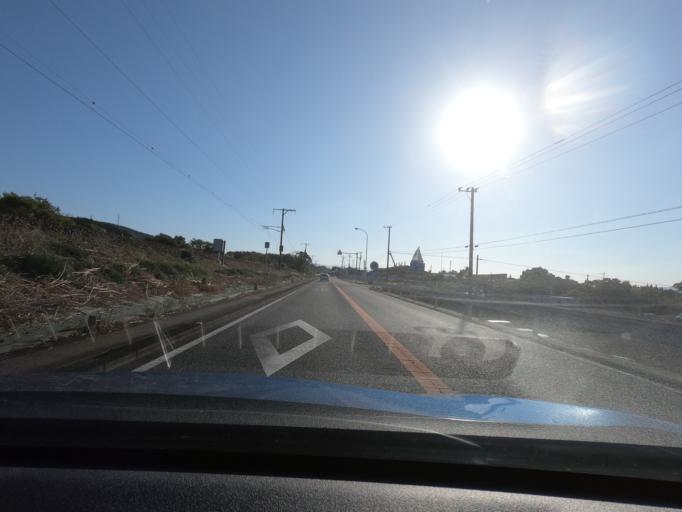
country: JP
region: Kagoshima
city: Izumi
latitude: 32.1439
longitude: 130.3562
